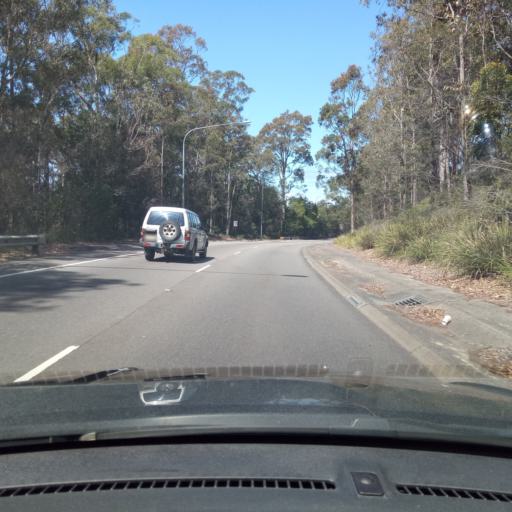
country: AU
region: New South Wales
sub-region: Wyong Shire
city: Chittaway Bay
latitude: -33.3318
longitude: 151.4312
